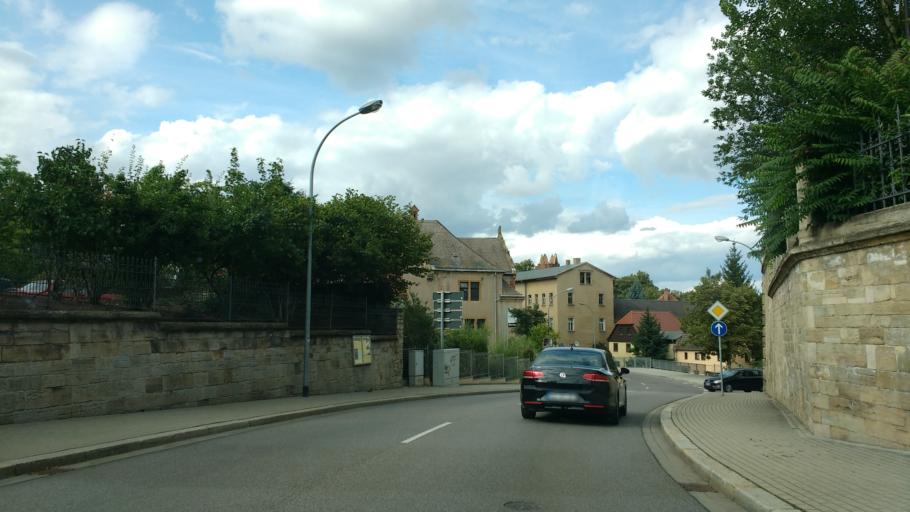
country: DE
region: Saxony-Anhalt
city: Zeitz
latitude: 51.0508
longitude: 12.1283
